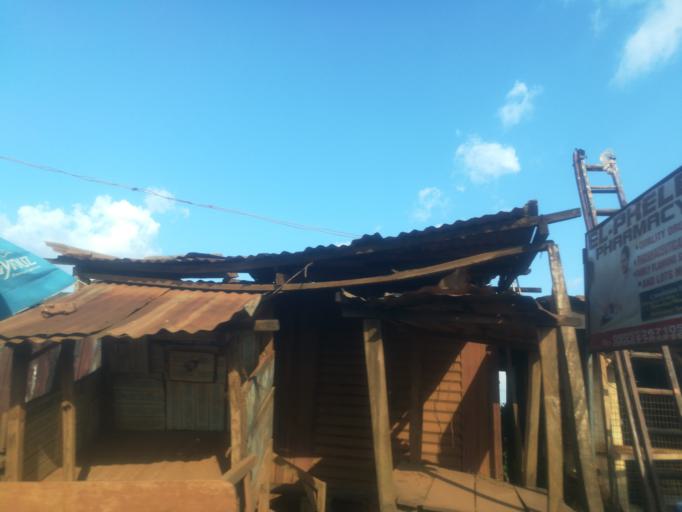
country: NG
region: Oyo
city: Lalupon
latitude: 7.4413
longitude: 3.9812
